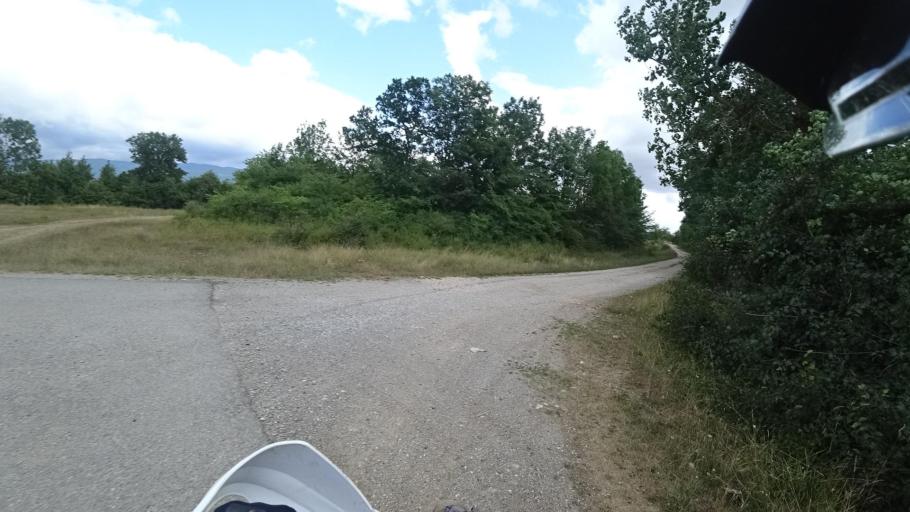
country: HR
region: Licko-Senjska
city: Jezerce
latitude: 44.6149
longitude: 15.6737
